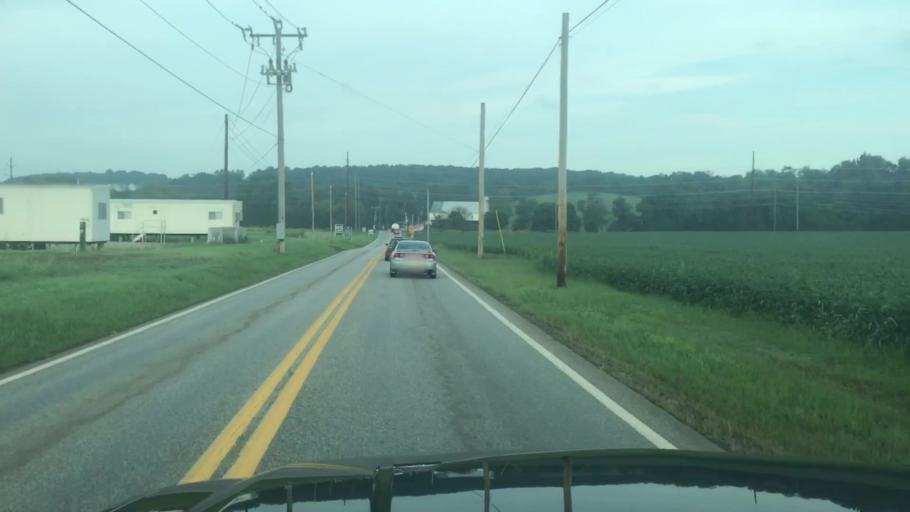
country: US
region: Pennsylvania
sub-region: Cumberland County
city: Shiremanstown
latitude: 40.1967
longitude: -76.9406
